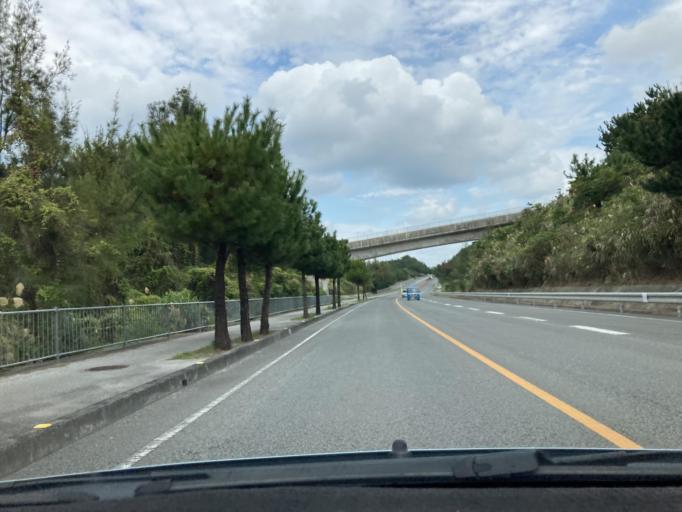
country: JP
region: Okinawa
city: Ishikawa
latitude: 26.4564
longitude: 127.8224
